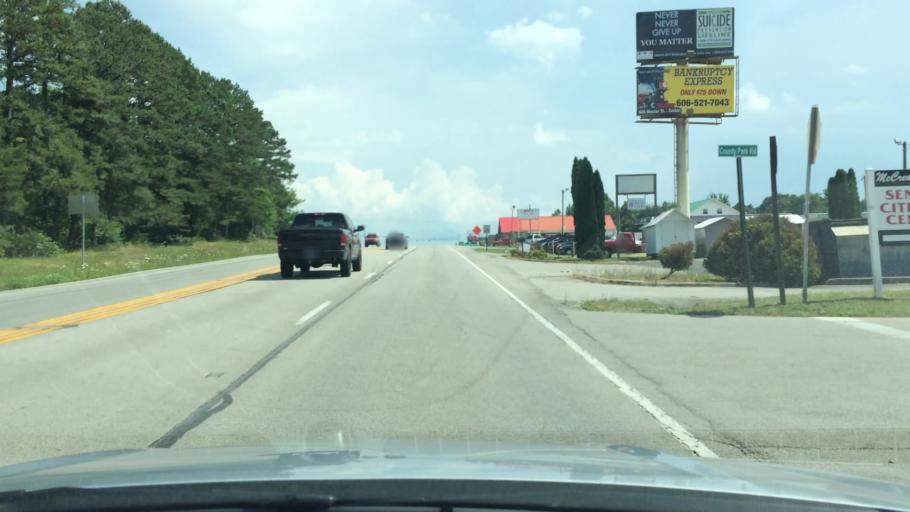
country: US
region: Kentucky
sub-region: McCreary County
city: Whitley City
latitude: 36.7505
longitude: -84.4748
